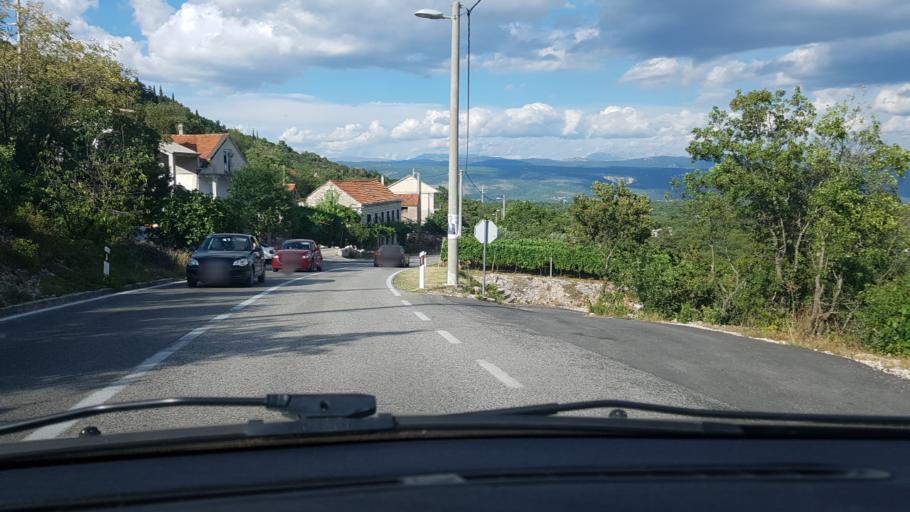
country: HR
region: Splitsko-Dalmatinska
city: Grubine
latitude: 43.4203
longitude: 17.1140
